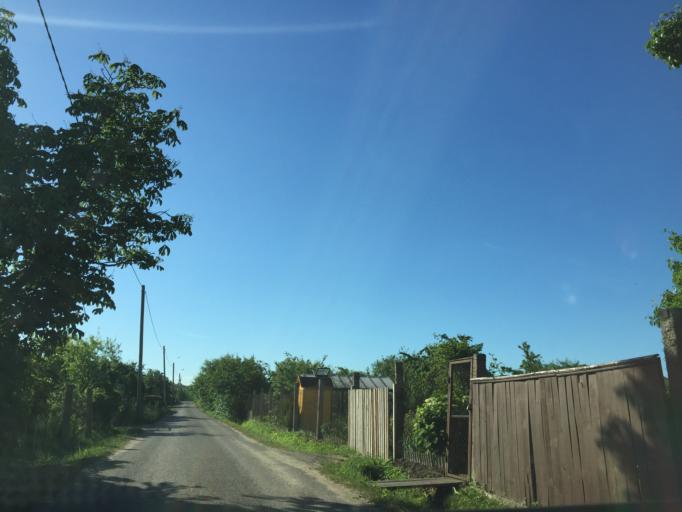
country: LV
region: Ventspils
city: Ventspils
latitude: 57.3702
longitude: 21.6061
